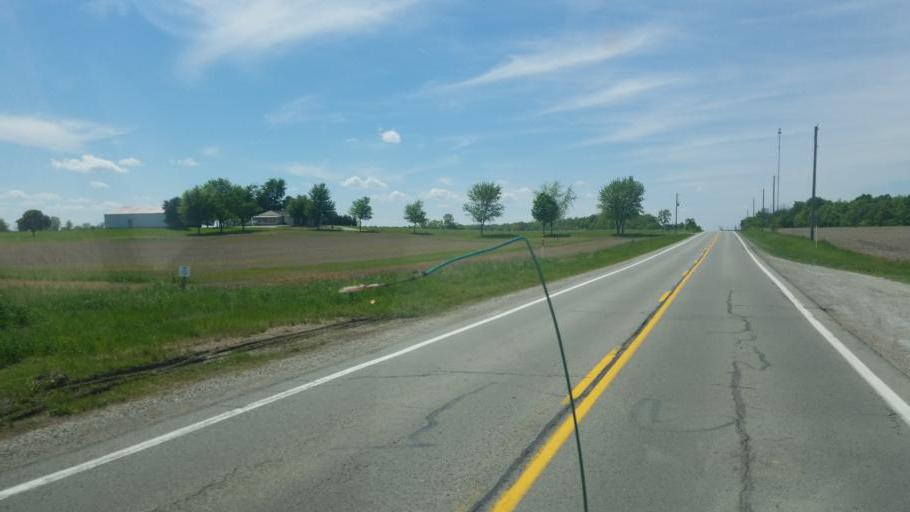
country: US
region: Ohio
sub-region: Huron County
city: Willard
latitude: 41.0713
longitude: -82.9045
